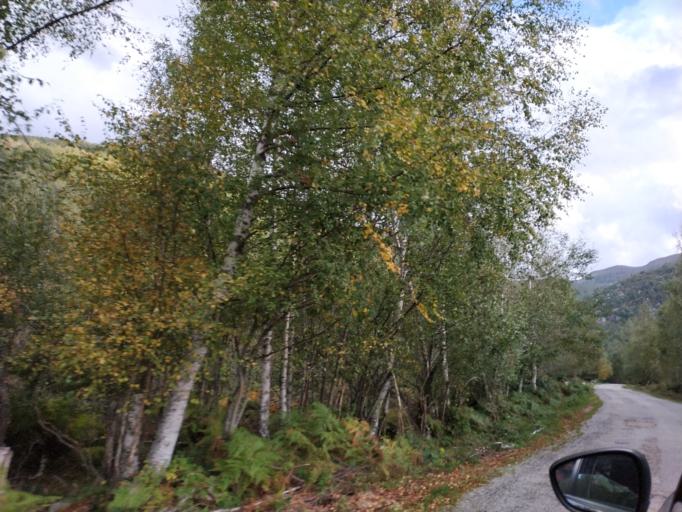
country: ES
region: Castille and Leon
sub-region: Provincia de Leon
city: Candin
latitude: 42.8619
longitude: -6.8564
